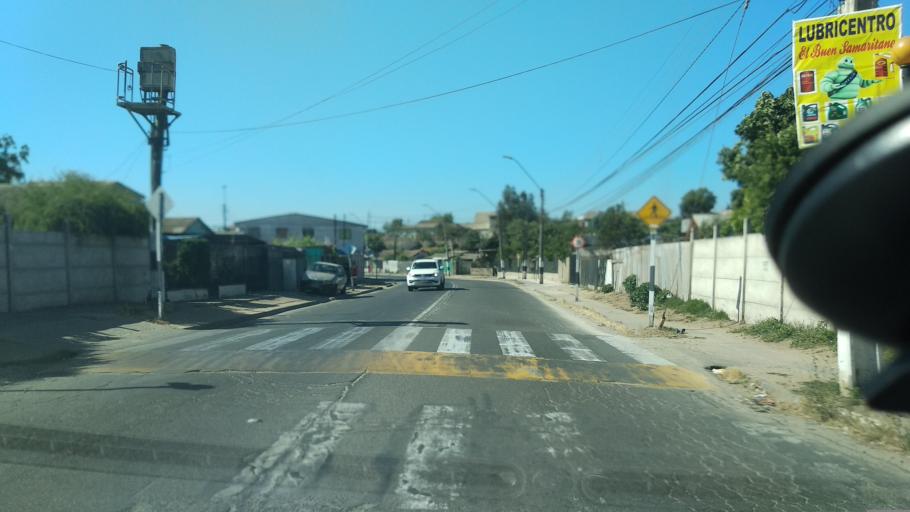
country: CL
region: Valparaiso
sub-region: Provincia de Marga Marga
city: Villa Alemana
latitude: -33.0624
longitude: -71.3711
